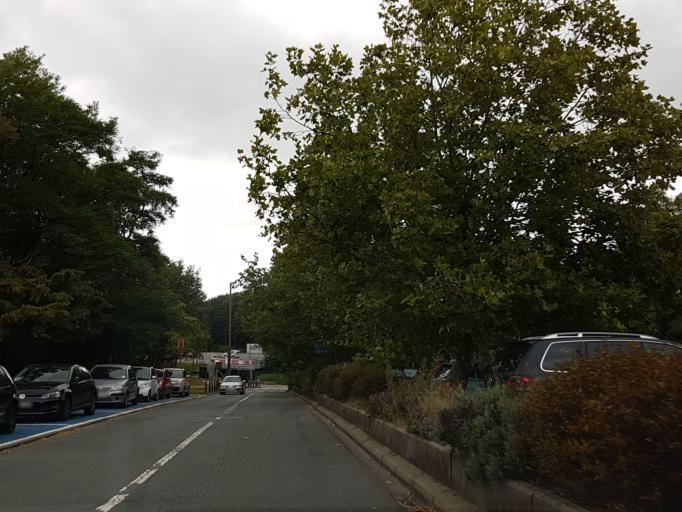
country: BE
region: Flanders
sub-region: Provincie Vlaams-Brabant
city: Kraainem
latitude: 50.8529
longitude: 4.4519
